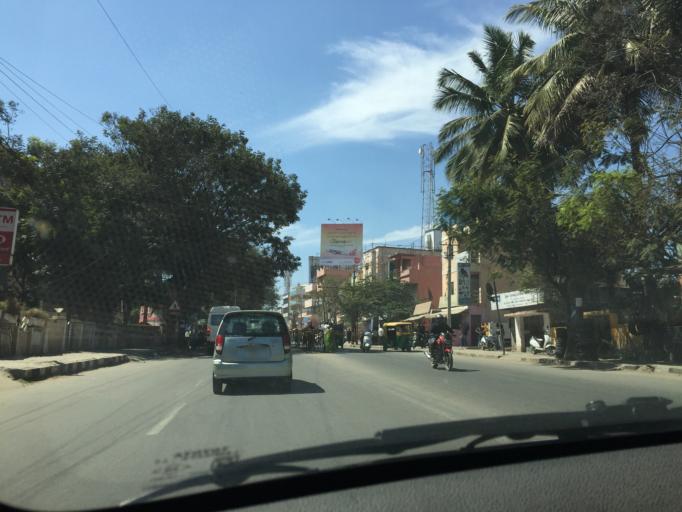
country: IN
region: Karnataka
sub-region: Bangalore Urban
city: Bangalore
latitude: 13.0136
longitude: 77.6266
